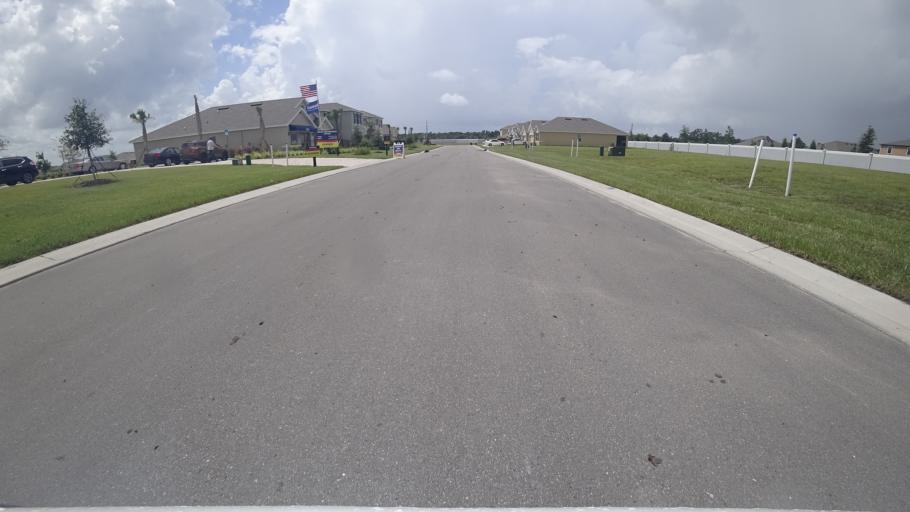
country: US
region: Florida
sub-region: Manatee County
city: Ellenton
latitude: 27.5486
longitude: -82.5152
